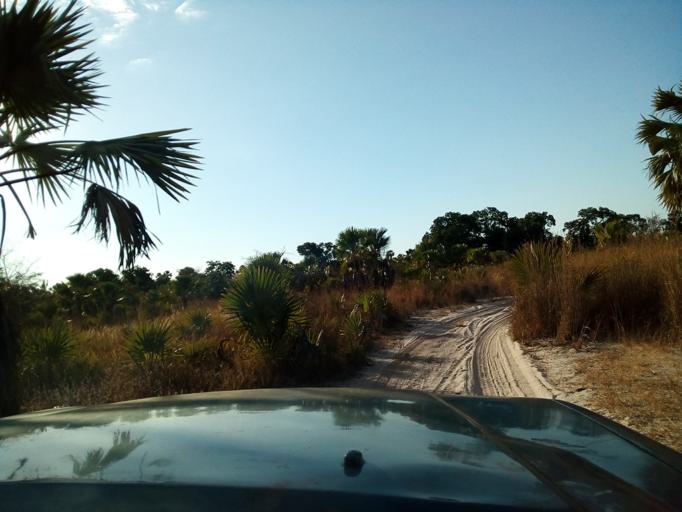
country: MG
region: Boeny
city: Sitampiky
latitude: -16.1279
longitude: 45.5428
